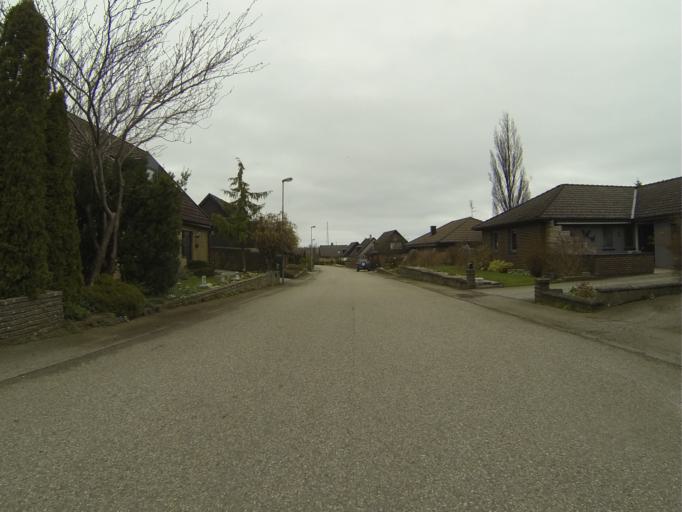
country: SE
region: Skane
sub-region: Simrishamns Kommun
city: Simrishamn
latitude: 55.5411
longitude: 14.3454
